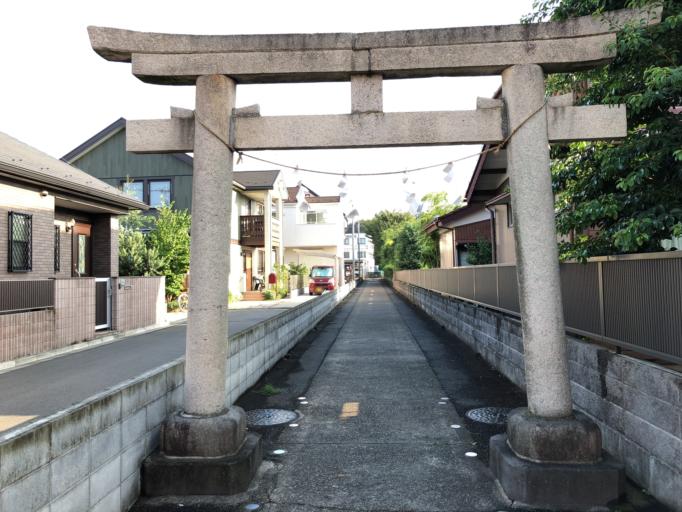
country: JP
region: Tokyo
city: Chofugaoka
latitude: 35.6689
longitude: 139.5051
